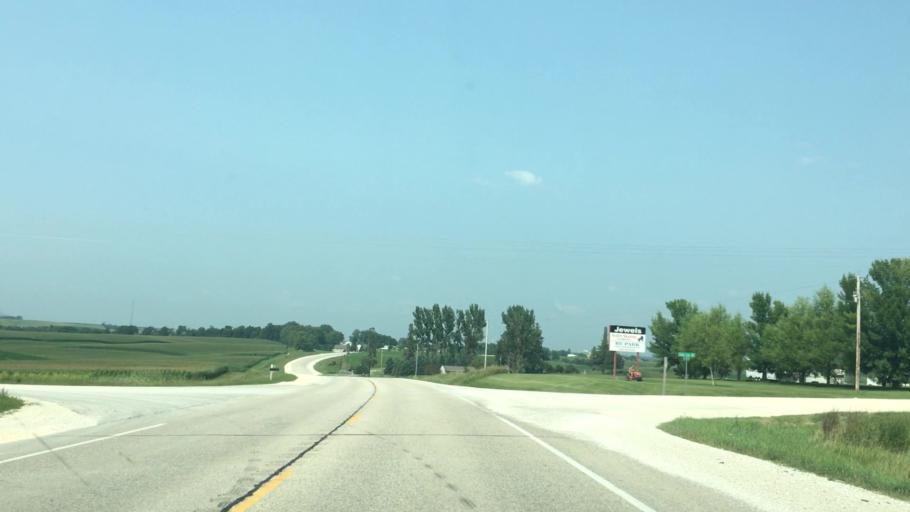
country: US
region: Iowa
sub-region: Winneshiek County
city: Decorah
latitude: 43.2550
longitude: -91.8385
